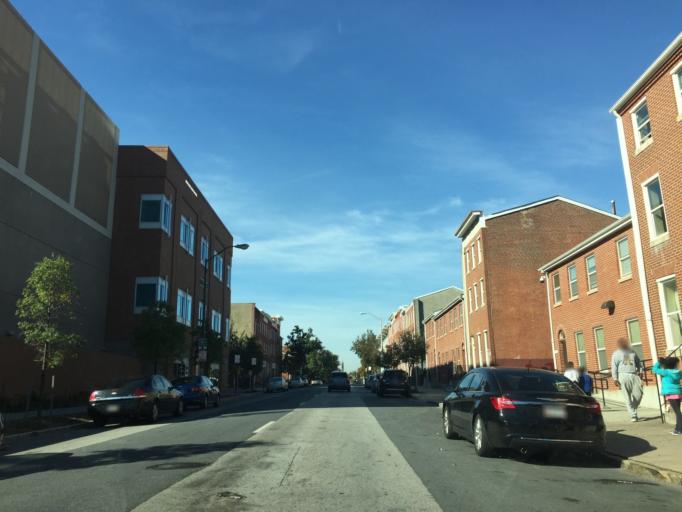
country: US
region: Maryland
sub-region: City of Baltimore
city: Baltimore
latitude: 39.2901
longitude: -76.6297
